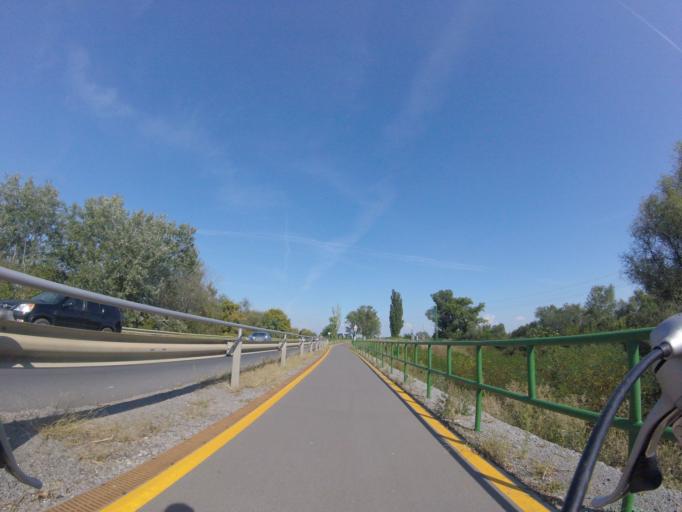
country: HU
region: Szabolcs-Szatmar-Bereg
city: Rakamaz
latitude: 48.1239
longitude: 21.4402
